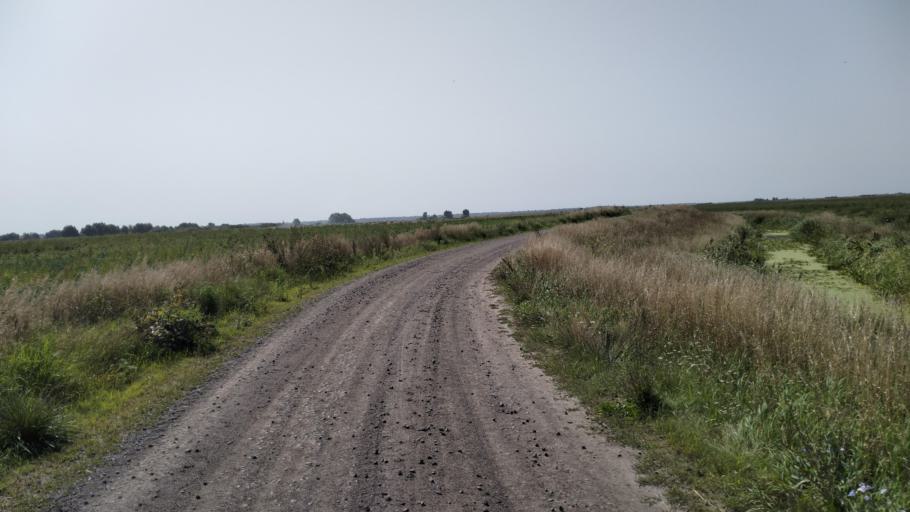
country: BY
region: Brest
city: Davyd-Haradok
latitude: 52.0069
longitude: 27.1670
